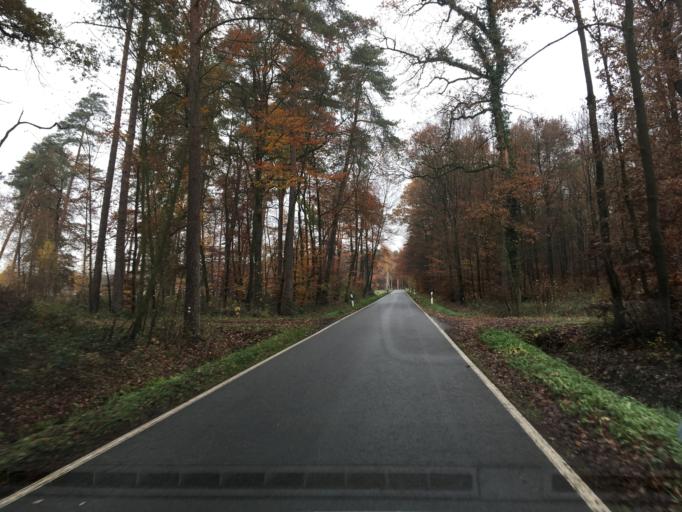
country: DE
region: North Rhine-Westphalia
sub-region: Regierungsbezirk Munster
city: Gescher
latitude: 51.9996
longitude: 6.9977
